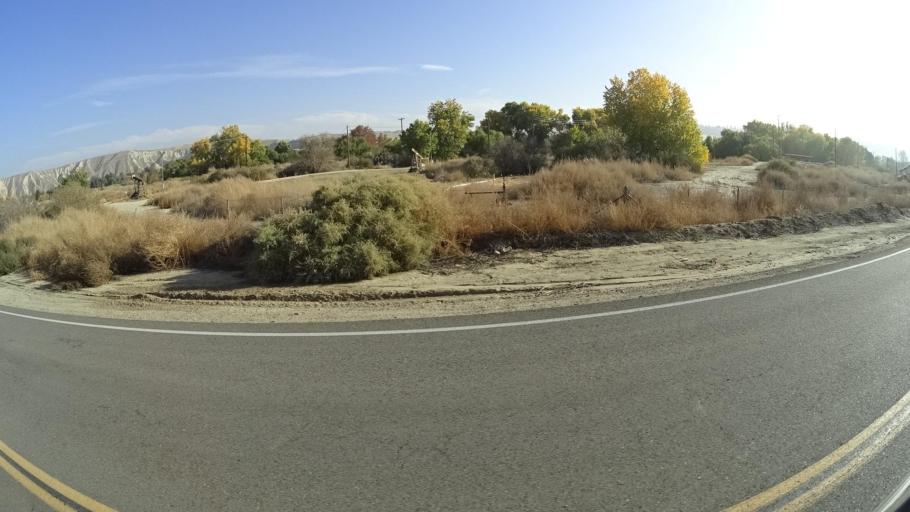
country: US
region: California
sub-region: Kern County
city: Oildale
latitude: 35.4342
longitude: -118.9517
